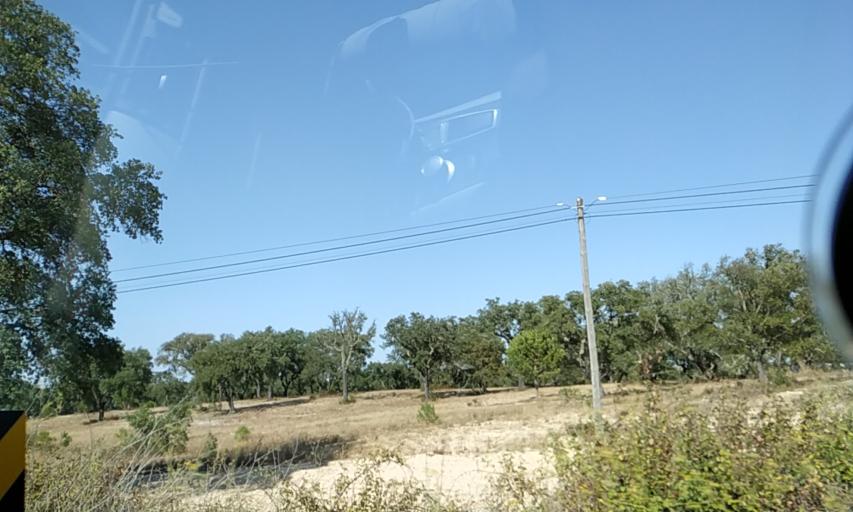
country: PT
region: Santarem
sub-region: Benavente
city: Poceirao
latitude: 38.7460
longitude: -8.6304
